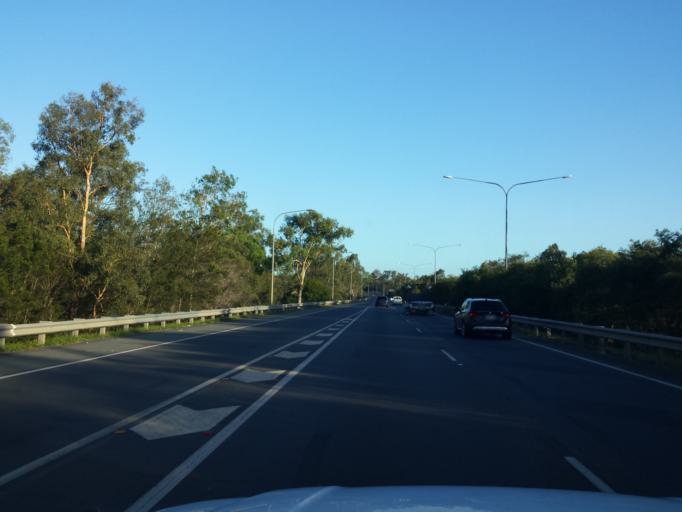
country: AU
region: Queensland
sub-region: Logan
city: Woodridge
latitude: -27.6538
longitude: 153.0730
